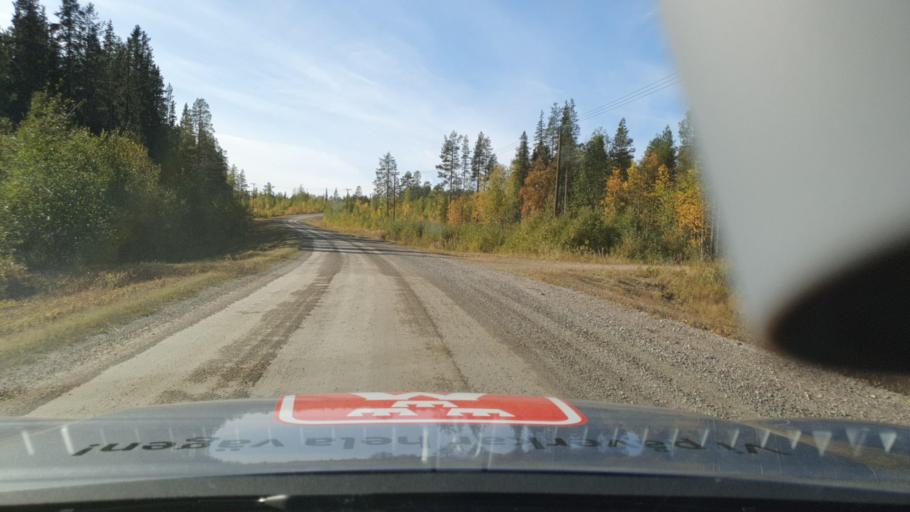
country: SE
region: Norrbotten
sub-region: Jokkmokks Kommun
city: Jokkmokk
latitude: 66.1570
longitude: 20.3414
